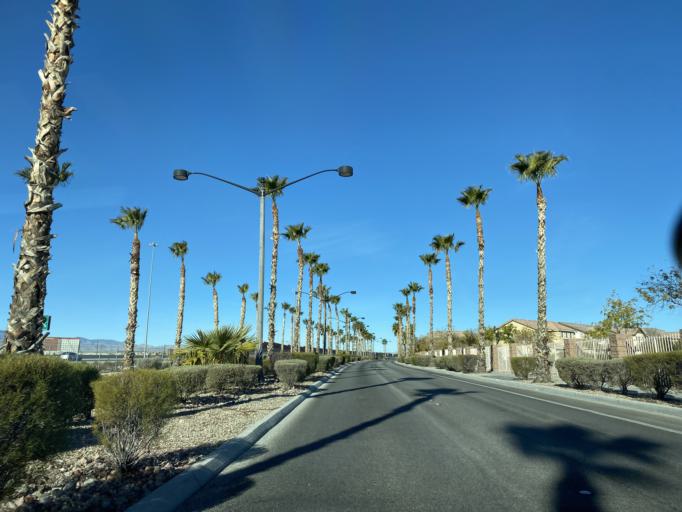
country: US
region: Nevada
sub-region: Clark County
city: Las Vegas
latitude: 36.2844
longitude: -115.2719
